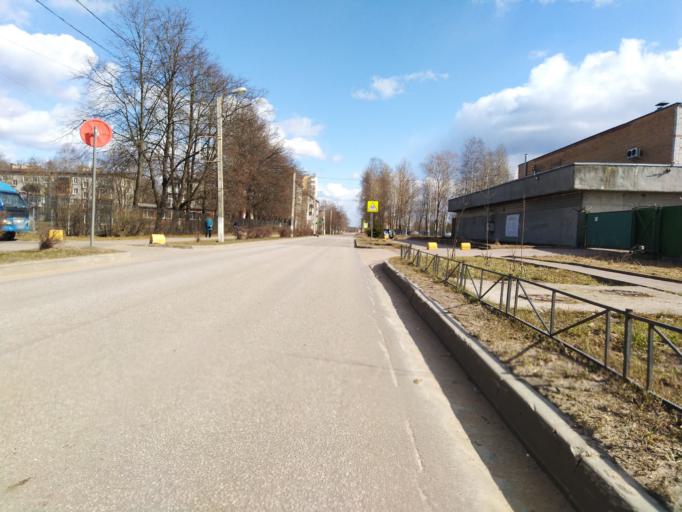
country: RU
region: Leningrad
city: Novoye Devyatkino
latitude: 60.1077
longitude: 30.4907
